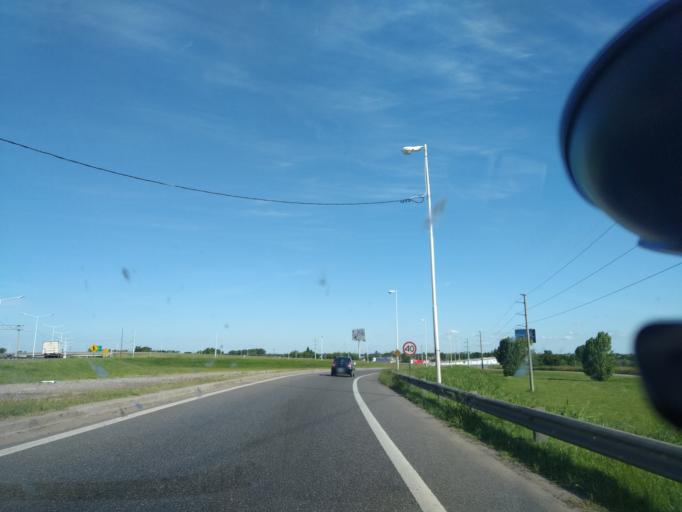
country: AR
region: Santa Fe
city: Gobernador Galvez
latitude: -33.0140
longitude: -60.6671
